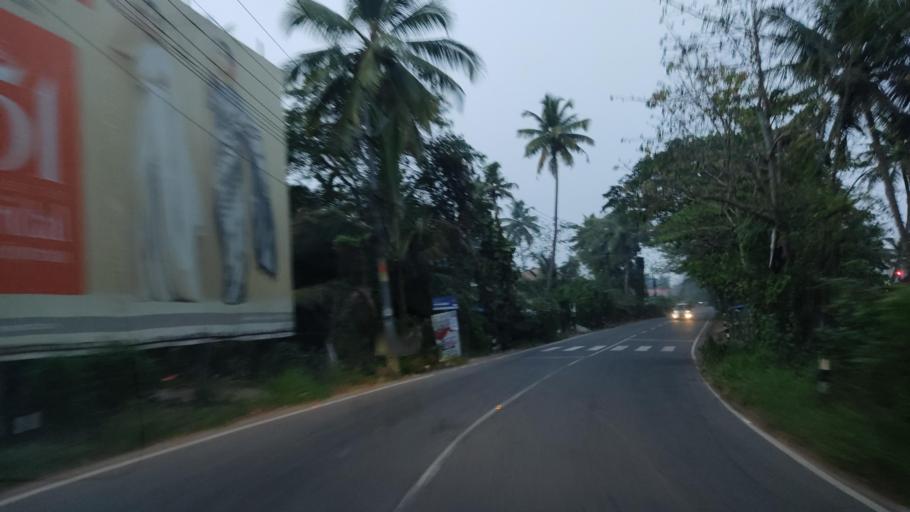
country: IN
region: Kerala
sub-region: Alappuzha
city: Shertallai
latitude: 9.6496
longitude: 76.4297
